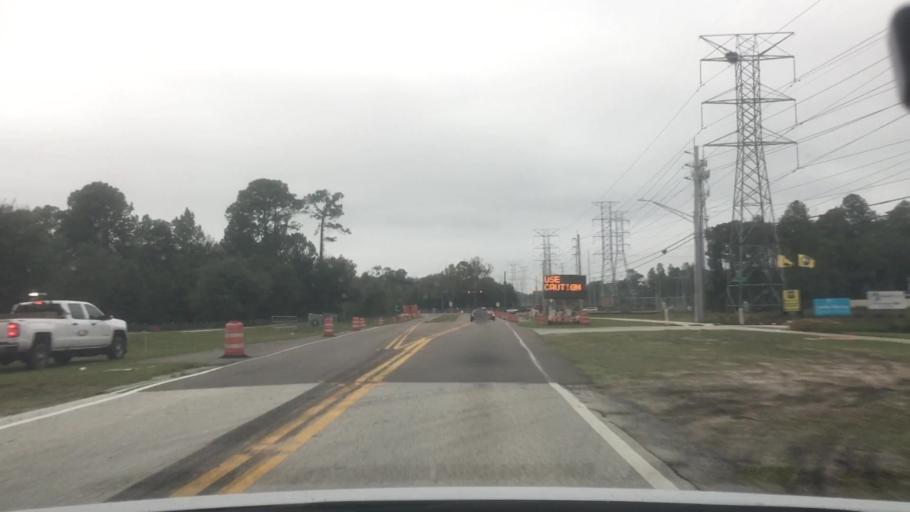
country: US
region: Florida
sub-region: Duval County
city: Atlantic Beach
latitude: 30.3572
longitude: -81.4901
